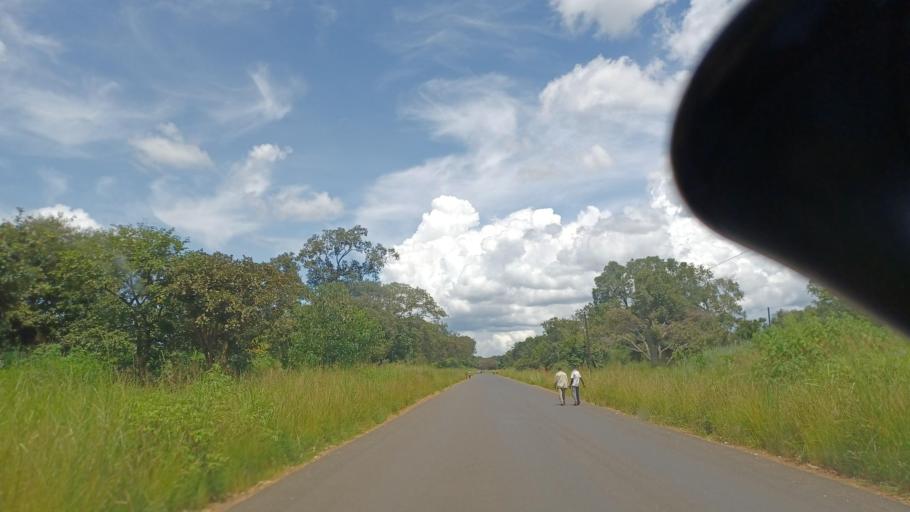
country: ZM
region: North-Western
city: Solwezi
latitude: -12.4007
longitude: 26.2393
